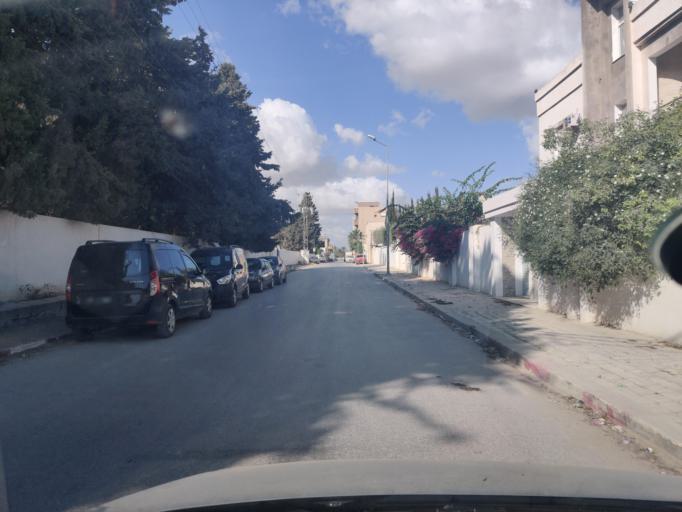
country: TN
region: Tunis
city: Al Marsa
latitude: 36.8780
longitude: 10.2699
